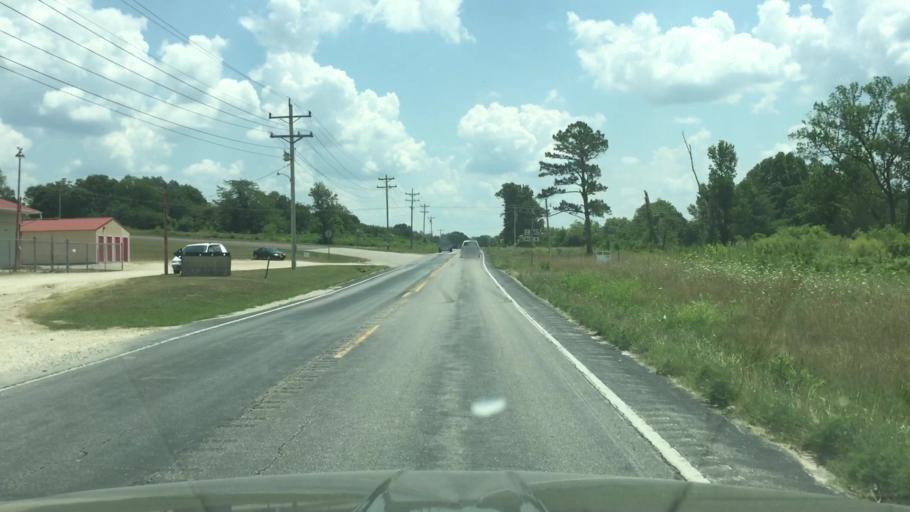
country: US
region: Missouri
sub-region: Miller County
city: Tuscumbia
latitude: 38.0855
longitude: -92.4907
